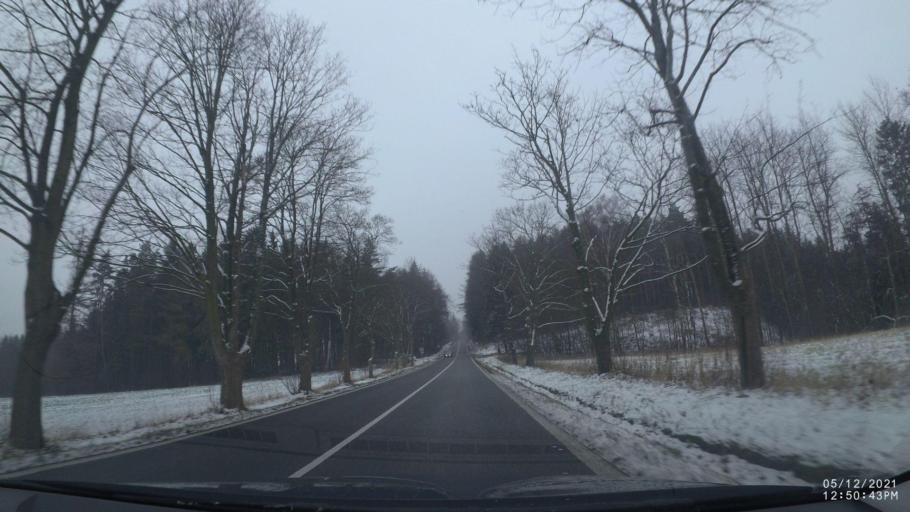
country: CZ
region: Kralovehradecky
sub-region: Okres Nachod
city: Nachod
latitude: 50.3890
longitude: 16.1414
